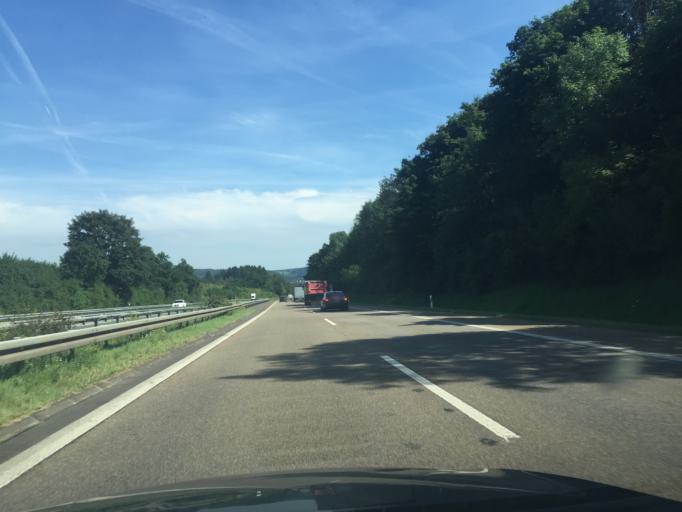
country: DE
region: North Rhine-Westphalia
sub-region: Regierungsbezirk Arnsberg
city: Drolshagen
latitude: 51.0376
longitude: 7.8094
